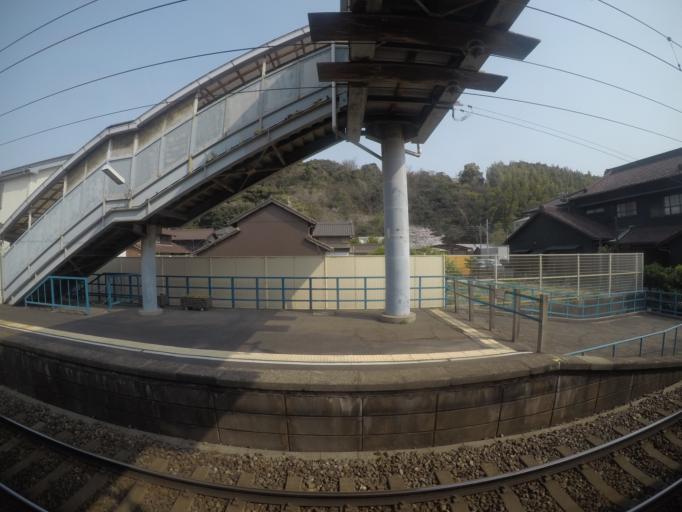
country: JP
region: Aichi
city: Obu
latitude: 35.0347
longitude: 136.8992
